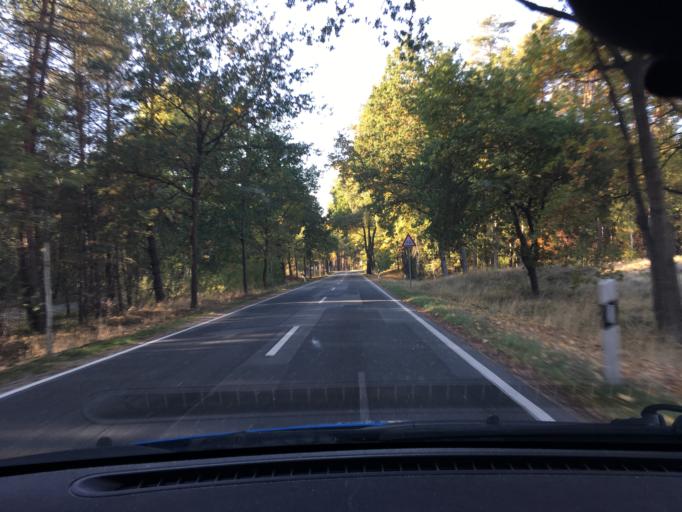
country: DE
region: Lower Saxony
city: Damnatz
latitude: 53.1584
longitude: 11.2016
